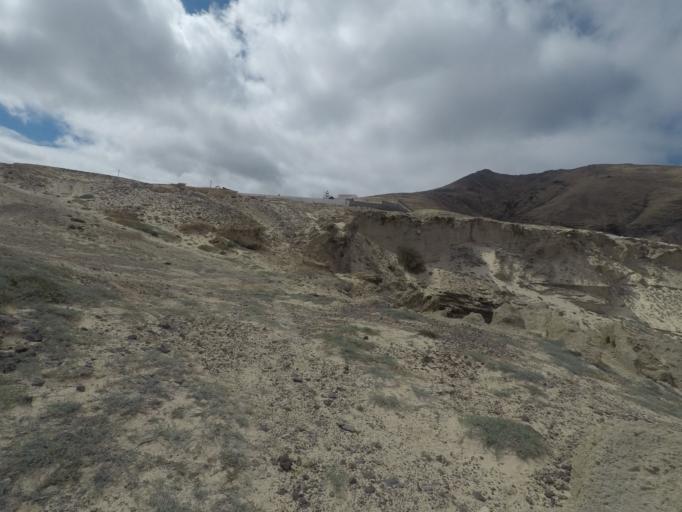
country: PT
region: Madeira
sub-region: Porto Santo
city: Vila de Porto Santo
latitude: 33.0712
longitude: -16.2969
